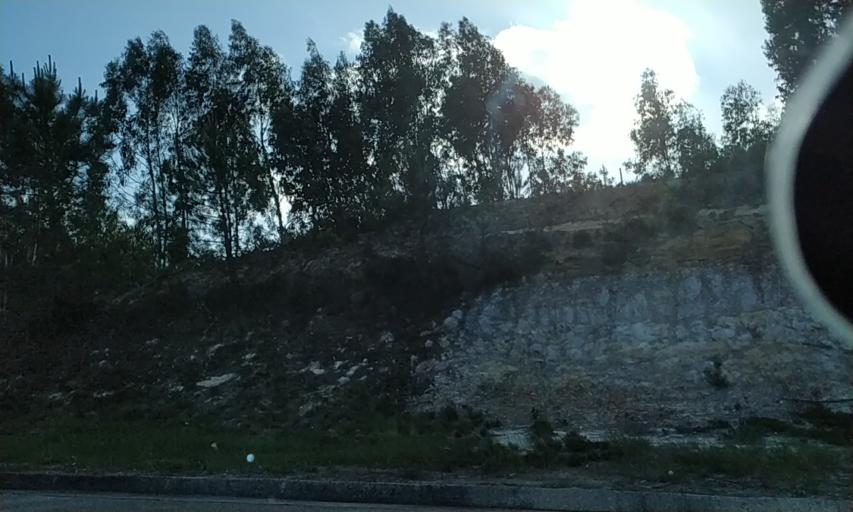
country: PT
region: Lisbon
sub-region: Torres Vedras
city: Torres Vedras
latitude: 39.1373
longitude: -9.2485
